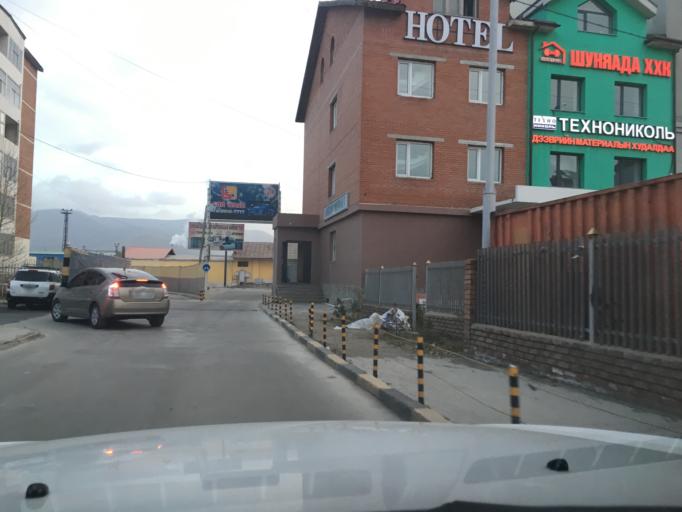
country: MN
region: Ulaanbaatar
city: Ulaanbaatar
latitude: 47.9123
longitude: 106.8618
